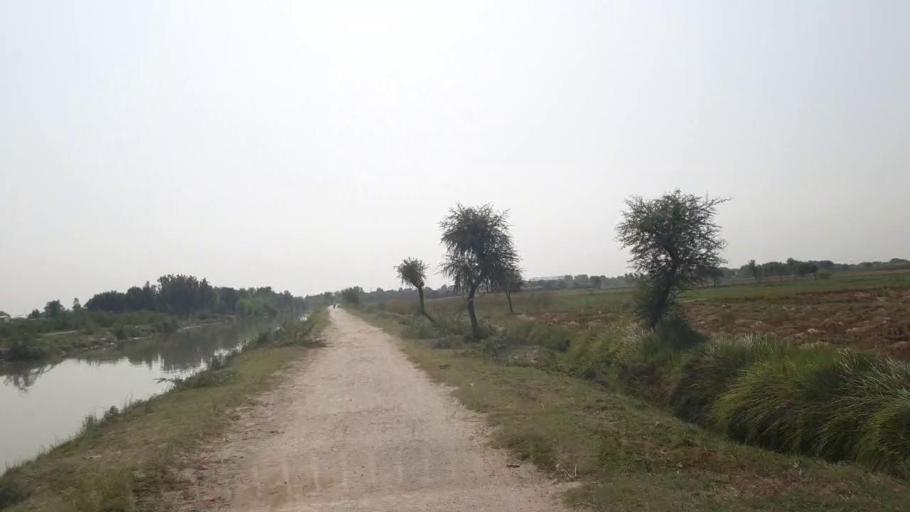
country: PK
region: Sindh
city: Badin
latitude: 24.6435
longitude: 68.8481
